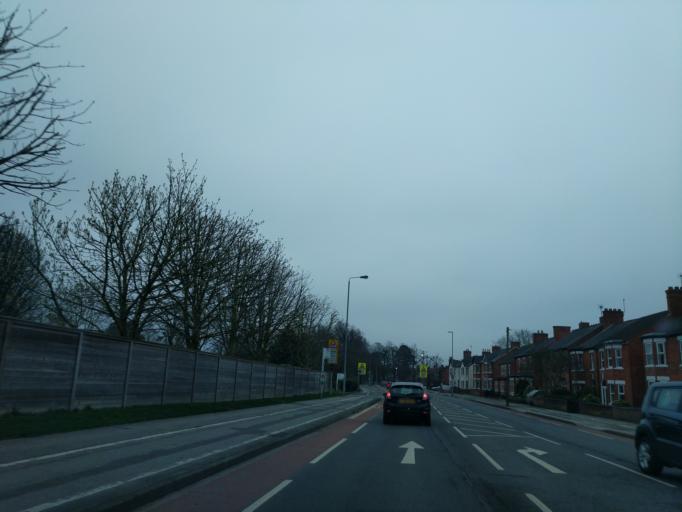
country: GB
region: England
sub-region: Nottinghamshire
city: Newark on Trent
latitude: 53.0640
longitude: -0.7899
